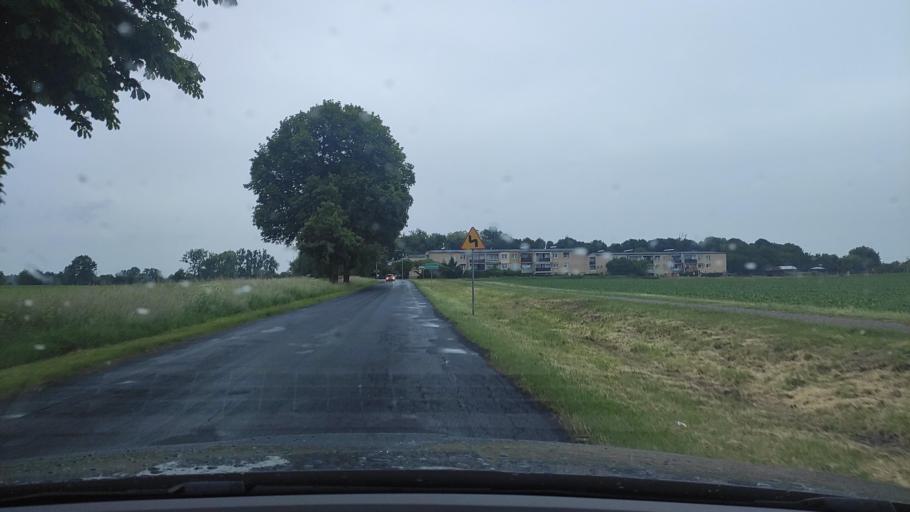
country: PL
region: Greater Poland Voivodeship
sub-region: Powiat poznanski
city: Kobylnica
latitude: 52.4919
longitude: 17.0972
